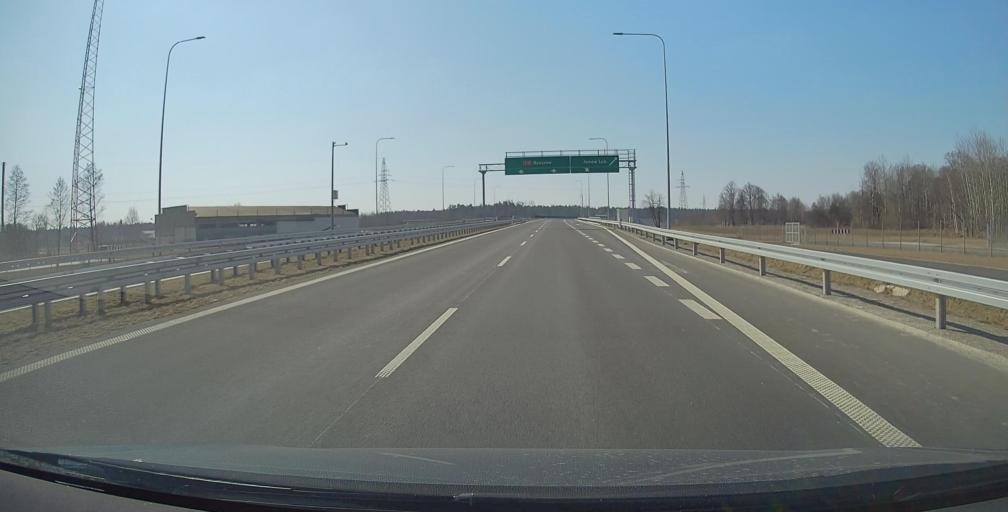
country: PL
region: Lublin Voivodeship
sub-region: Powiat janowski
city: Janow Lubelski
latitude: 50.6983
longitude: 22.3793
